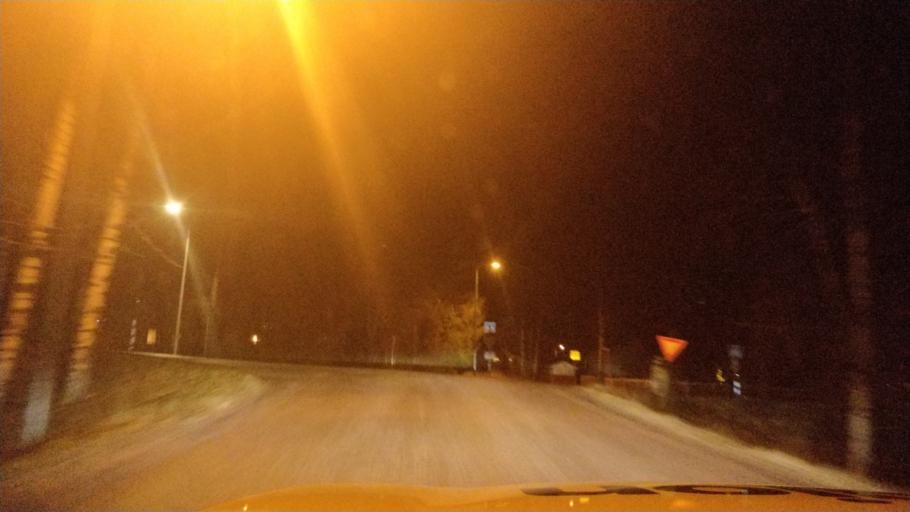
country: FI
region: Uusimaa
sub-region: Helsinki
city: Nurmijaervi
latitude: 60.3822
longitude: 24.6955
